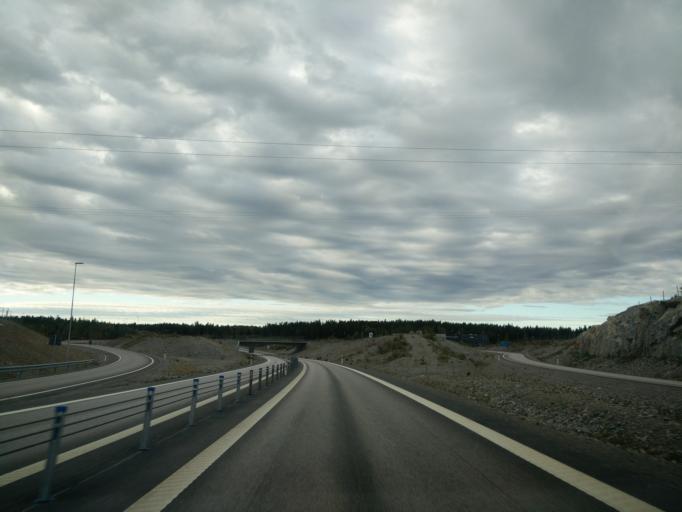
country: SE
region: Gaevleborg
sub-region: Hudiksvalls Kommun
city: Hudiksvall
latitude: 61.7166
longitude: 17.0505
